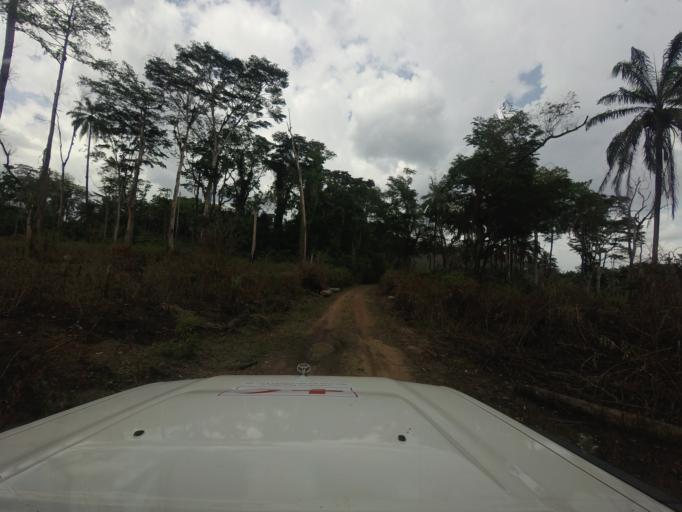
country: LR
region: Lofa
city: Voinjama
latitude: 8.3936
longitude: -9.6002
